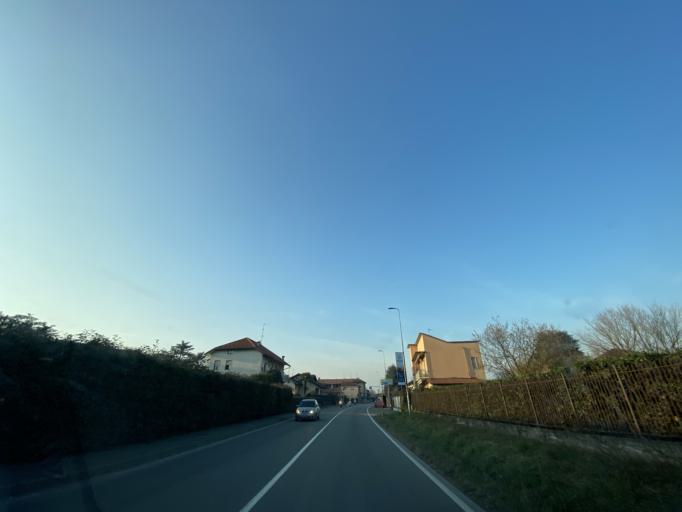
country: IT
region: Lombardy
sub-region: Citta metropolitana di Milano
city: Passirana
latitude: 45.5478
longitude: 9.0314
